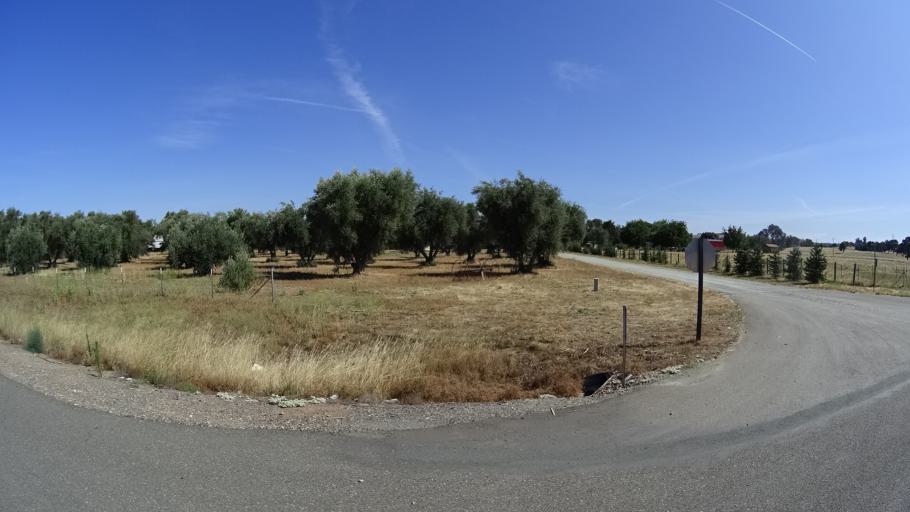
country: US
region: California
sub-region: Calaveras County
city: Rancho Calaveras
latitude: 38.1048
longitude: -120.9144
